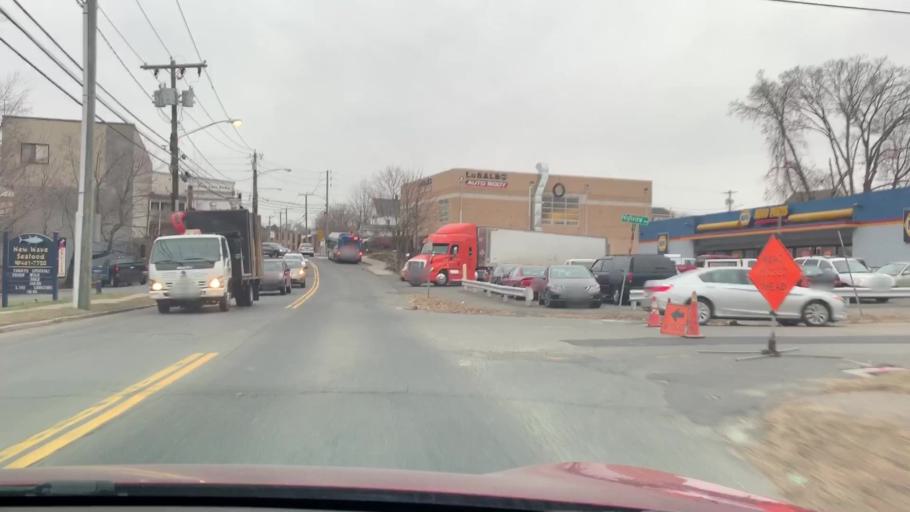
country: US
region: Connecticut
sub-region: Fairfield County
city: Stamford
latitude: 41.0954
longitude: -73.5159
